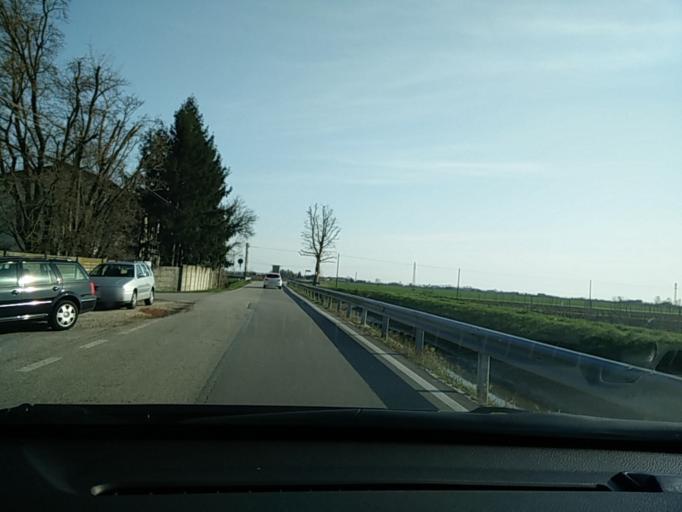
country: IT
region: Veneto
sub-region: Provincia di Venezia
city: Musile di Piave
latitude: 45.6150
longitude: 12.5309
